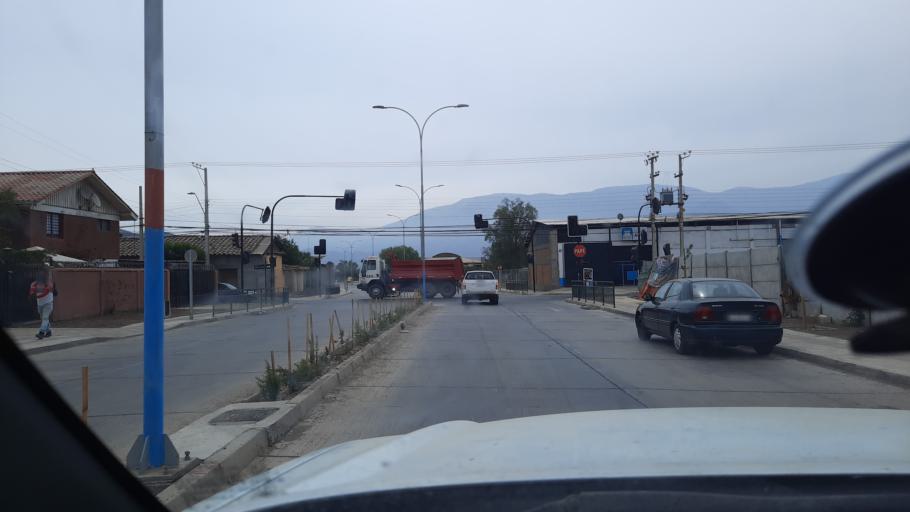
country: CL
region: Valparaiso
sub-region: Provincia de San Felipe
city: San Felipe
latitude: -32.7427
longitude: -70.7209
